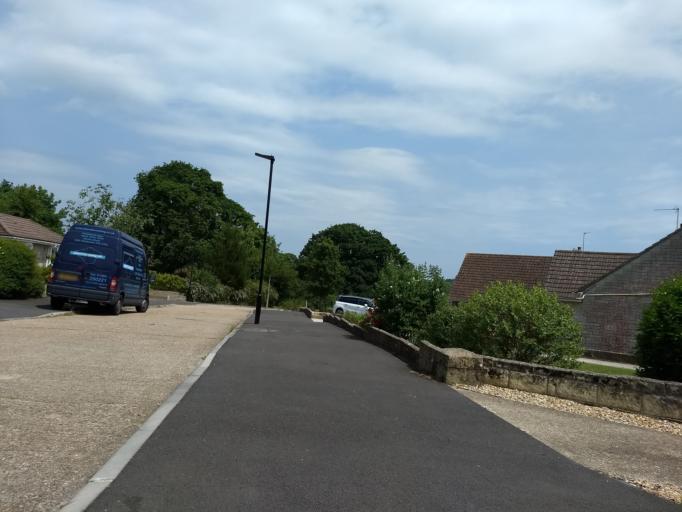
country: GB
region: England
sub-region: Isle of Wight
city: Seaview
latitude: 50.7163
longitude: -1.1289
